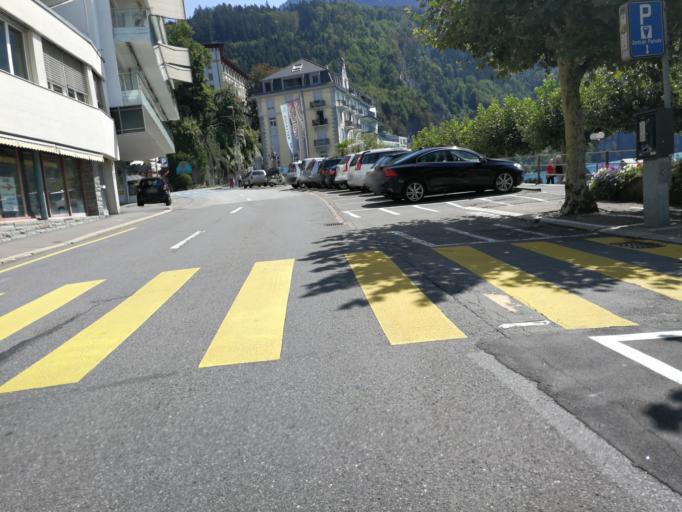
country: CH
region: Schwyz
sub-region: Bezirk Schwyz
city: Ingenbohl
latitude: 46.9936
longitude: 8.6063
